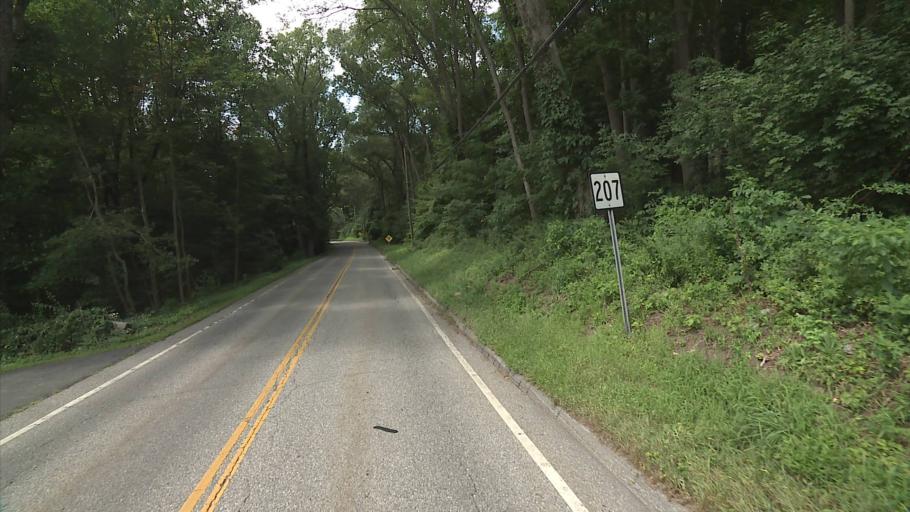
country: US
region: Connecticut
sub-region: Windham County
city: South Windham
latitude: 41.6433
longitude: -72.1884
